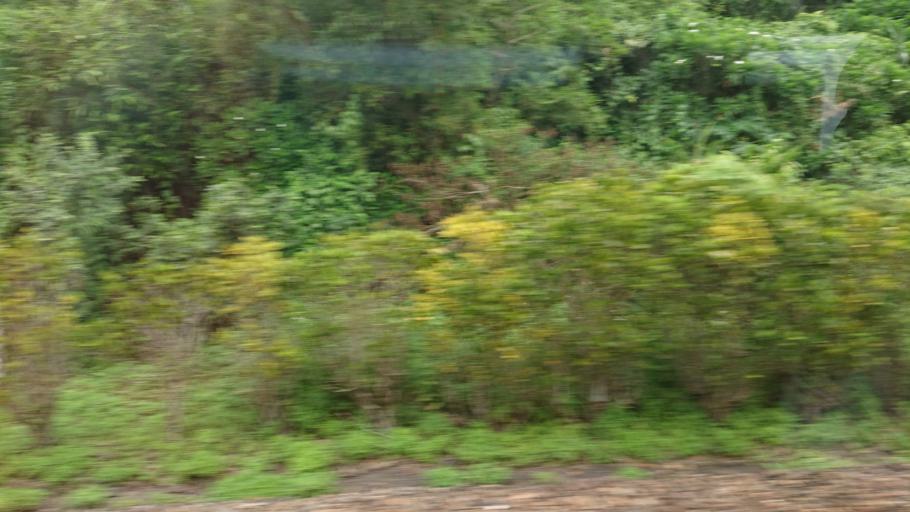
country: TW
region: Taiwan
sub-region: Yilan
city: Yilan
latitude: 24.9103
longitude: 121.8755
